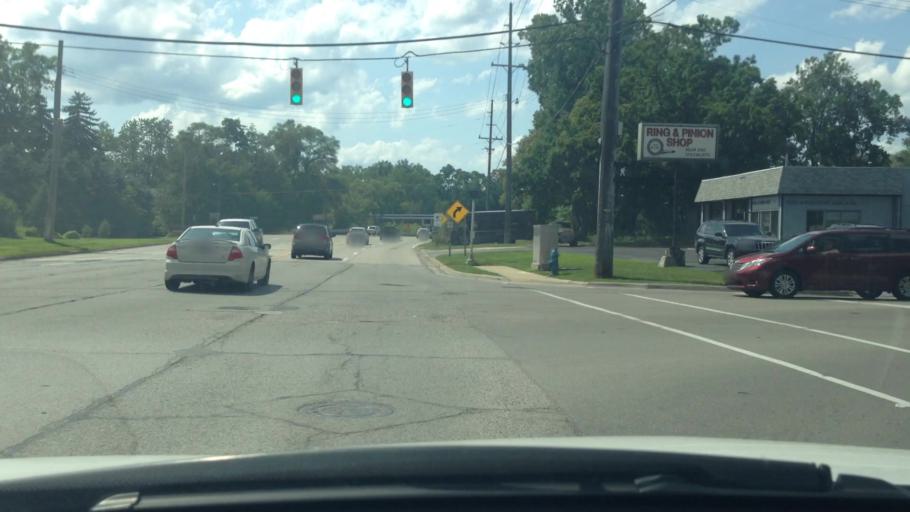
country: US
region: Michigan
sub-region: Oakland County
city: Waterford
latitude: 42.6879
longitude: -83.3499
